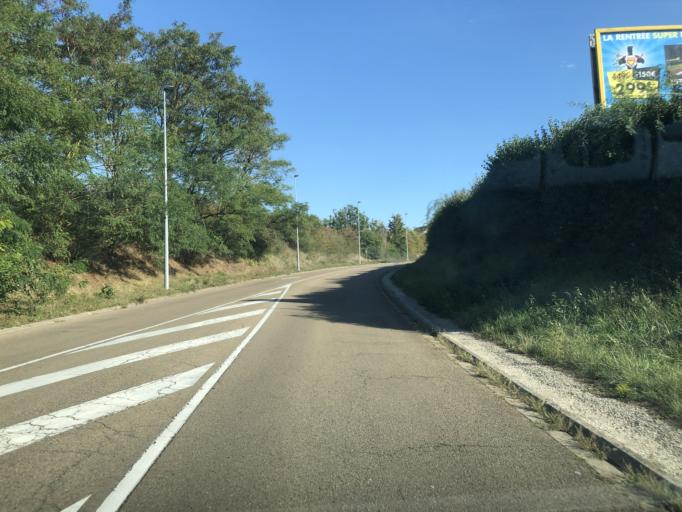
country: FR
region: Bourgogne
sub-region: Departement de l'Yonne
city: Auxerre
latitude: 47.8057
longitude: 3.5894
